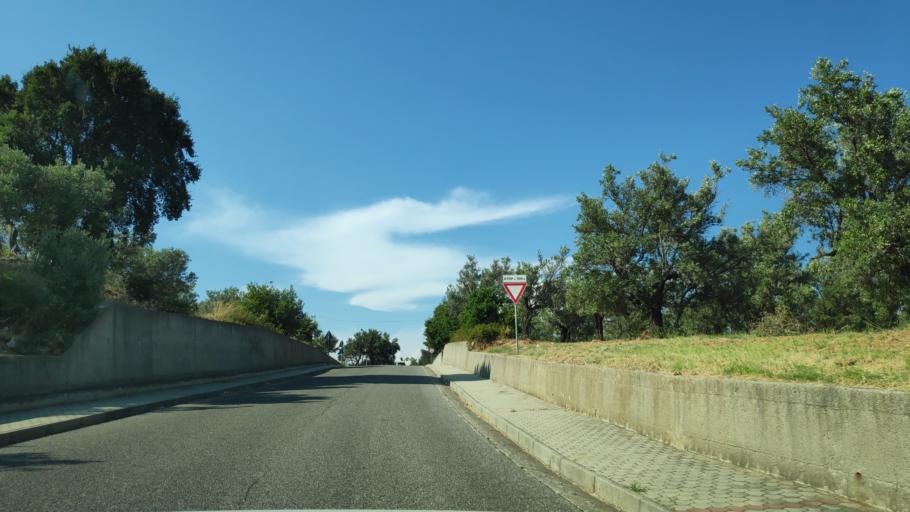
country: IT
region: Calabria
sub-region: Provincia di Catanzaro
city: Soverato Superiore
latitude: 38.6866
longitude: 16.5367
